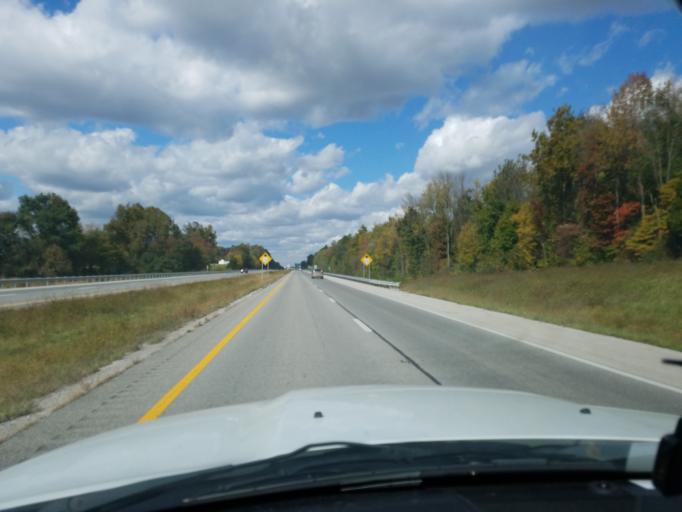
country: US
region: Kentucky
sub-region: Daviess County
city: Masonville
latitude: 37.7250
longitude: -87.0579
